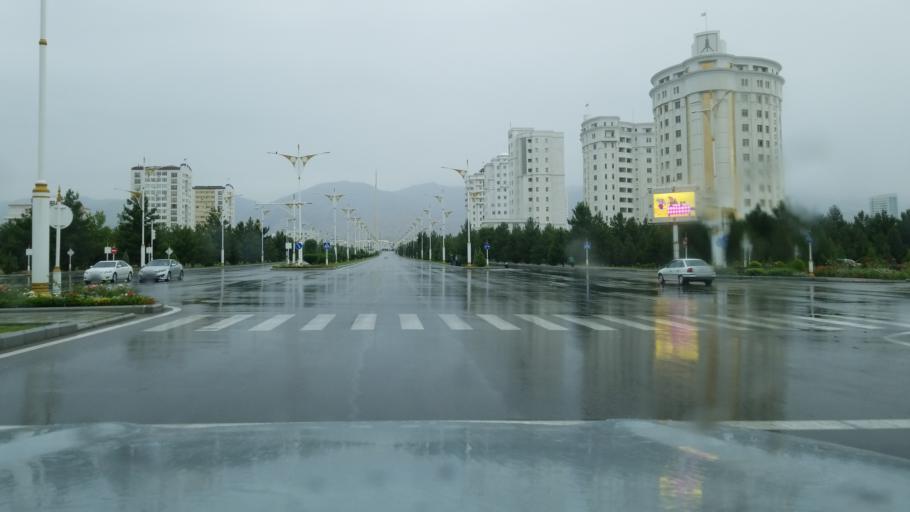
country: TM
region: Ahal
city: Ashgabat
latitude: 37.8955
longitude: 58.3579
